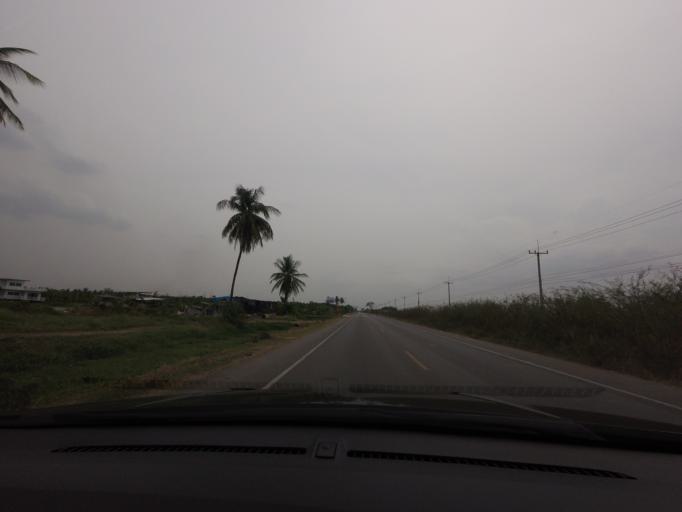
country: TH
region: Phetchaburi
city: Ban Laem
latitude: 13.1778
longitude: 99.9368
